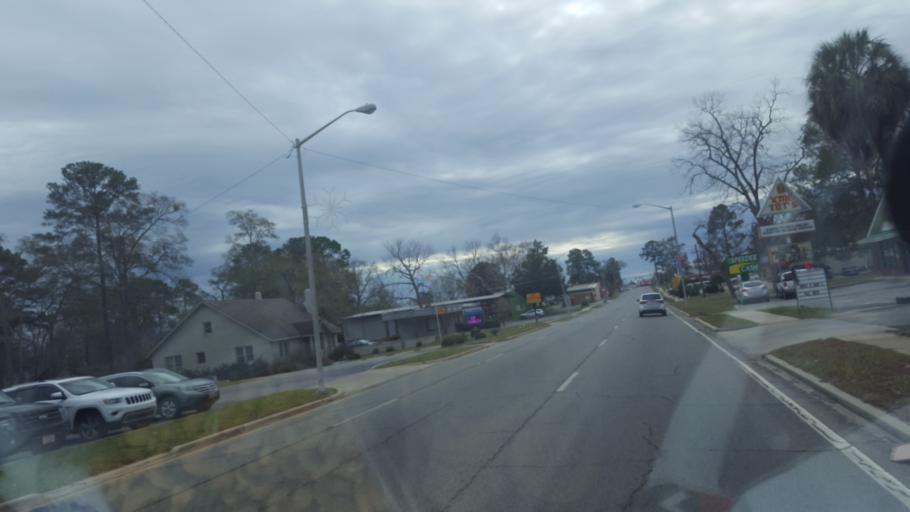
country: US
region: Georgia
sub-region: Ben Hill County
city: Fitzgerald
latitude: 31.7101
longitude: -83.2529
